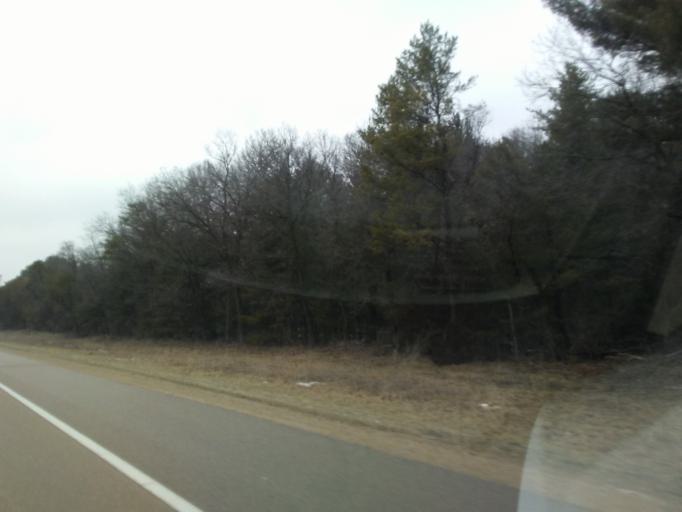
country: US
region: Wisconsin
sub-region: Sauk County
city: Spring Green
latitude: 43.1913
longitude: -90.1855
